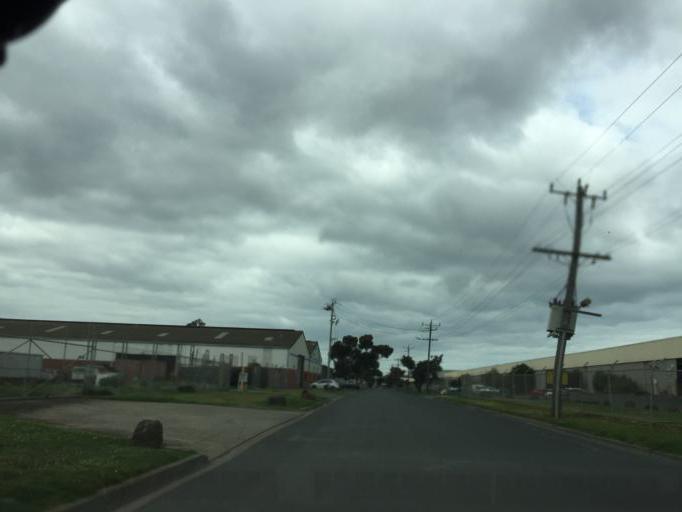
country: AU
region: Victoria
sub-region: Brimbank
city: Brooklyn
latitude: -37.8026
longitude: 144.8484
